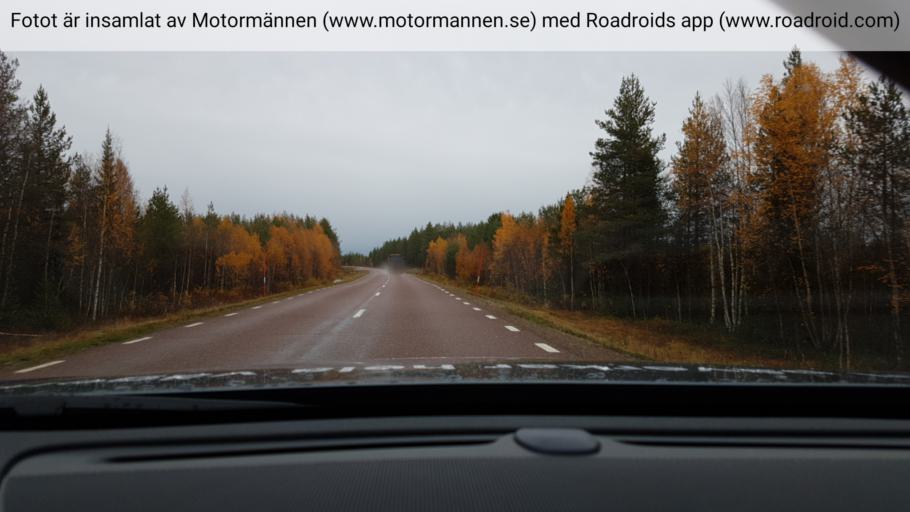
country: SE
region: Norrbotten
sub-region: Pajala Kommun
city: Pajala
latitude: 67.1690
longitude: 22.6697
